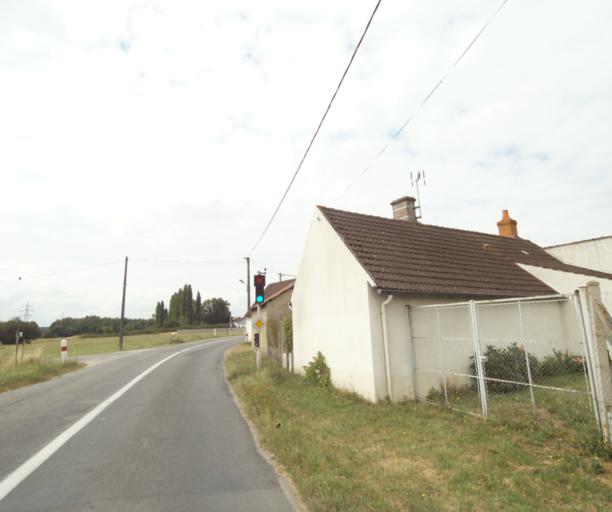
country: FR
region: Centre
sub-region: Departement du Loiret
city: Boigny-sur-Bionne
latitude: 47.9180
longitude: 2.0424
